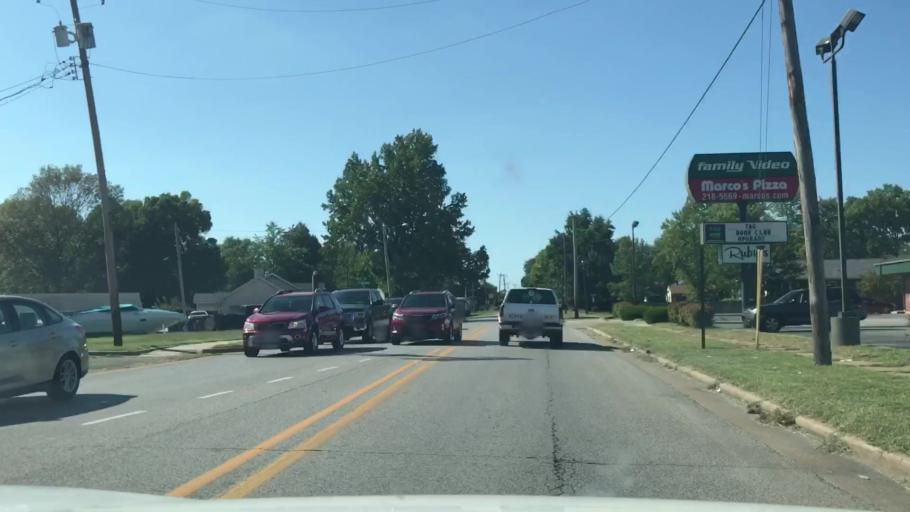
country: US
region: Illinois
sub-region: Madison County
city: Wood River
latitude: 38.8655
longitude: -90.0825
